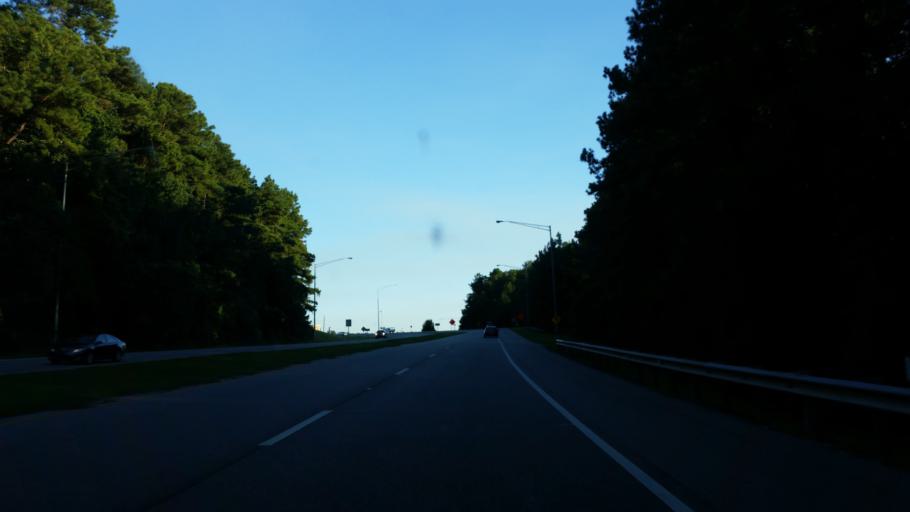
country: US
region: Alabama
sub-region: Baldwin County
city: Spanish Fort
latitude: 30.6605
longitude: -87.9133
